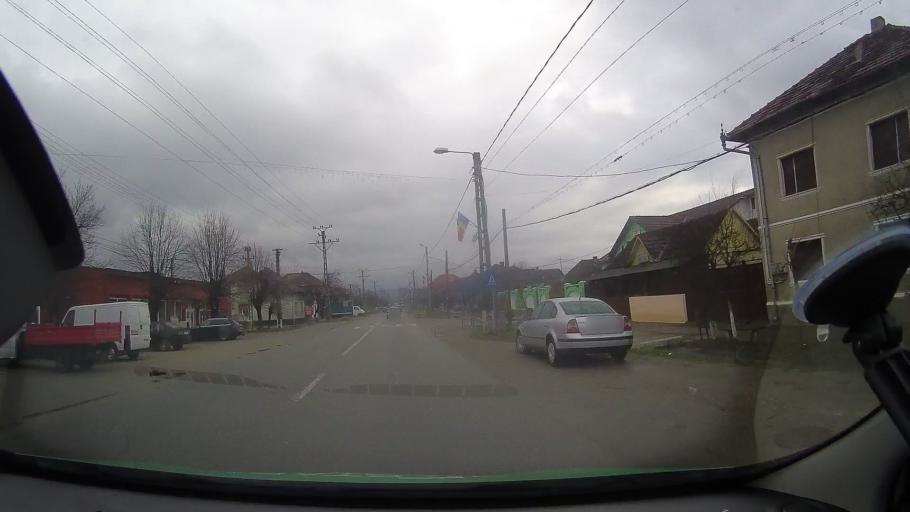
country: RO
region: Arad
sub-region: Comuna Sebis
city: Sebis
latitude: 46.3671
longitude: 22.1309
